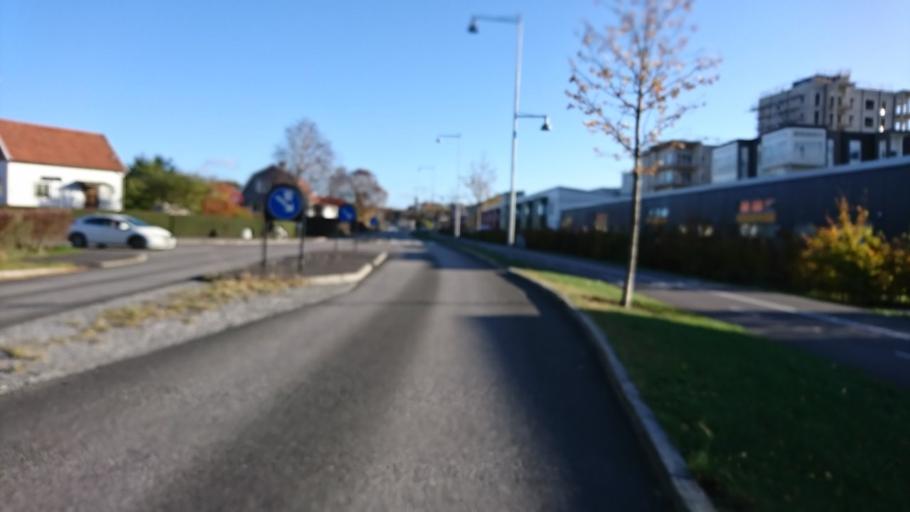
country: SE
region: Vaestra Goetaland
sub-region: Molndal
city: Moelndal
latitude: 57.6523
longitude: 11.9973
